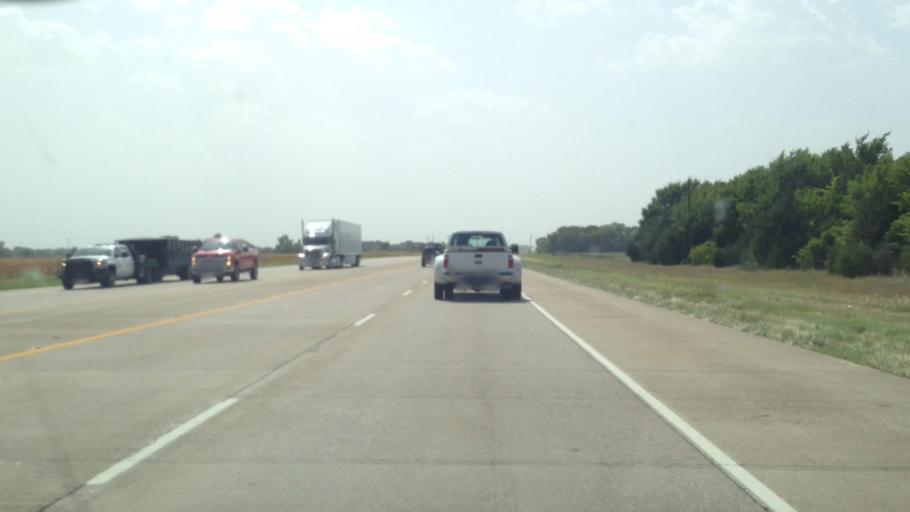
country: US
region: Texas
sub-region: Collin County
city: Princeton
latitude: 33.1649
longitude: -96.4480
